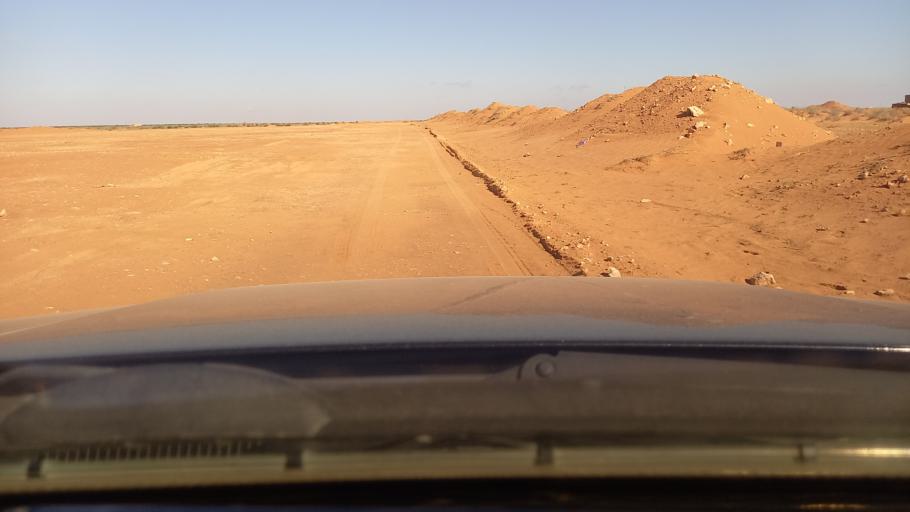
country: TN
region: Madanin
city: Medenine
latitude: 33.1742
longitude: 10.5277
